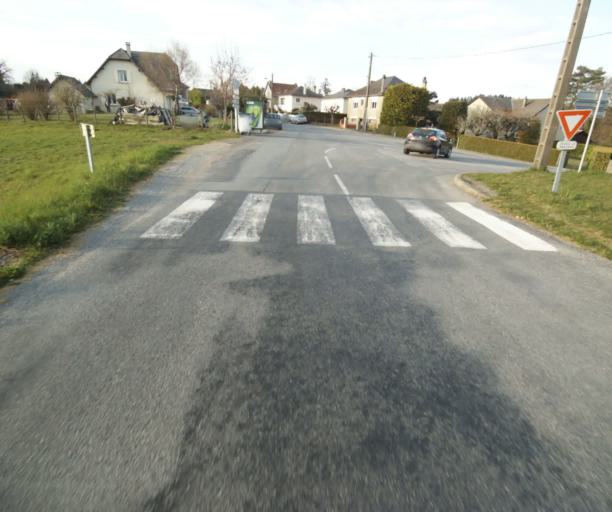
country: FR
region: Limousin
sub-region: Departement de la Correze
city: Correze
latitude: 45.3762
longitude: 1.8655
